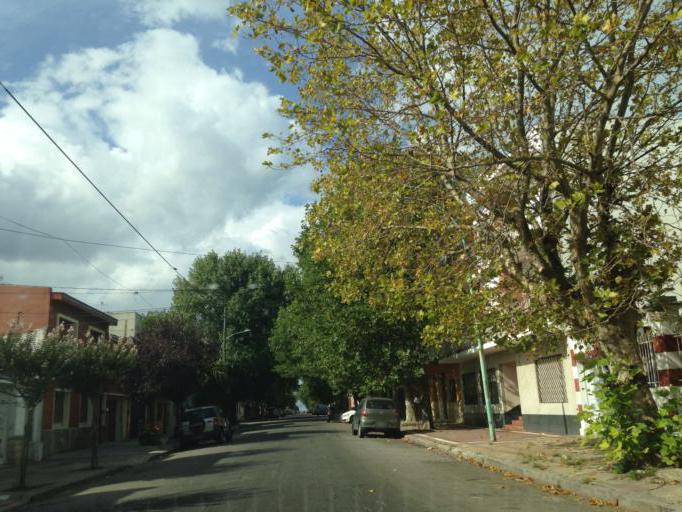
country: AR
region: Buenos Aires
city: Mar del Plata
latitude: -37.9878
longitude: -57.5490
